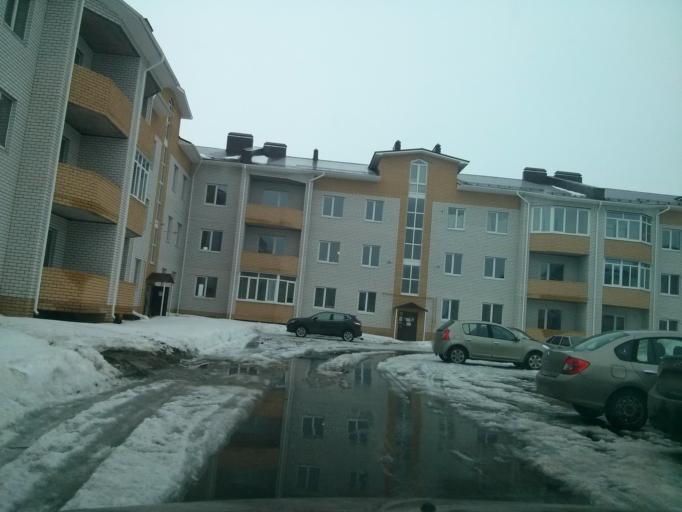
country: RU
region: Vladimir
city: Murom
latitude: 55.5459
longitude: 42.0596
